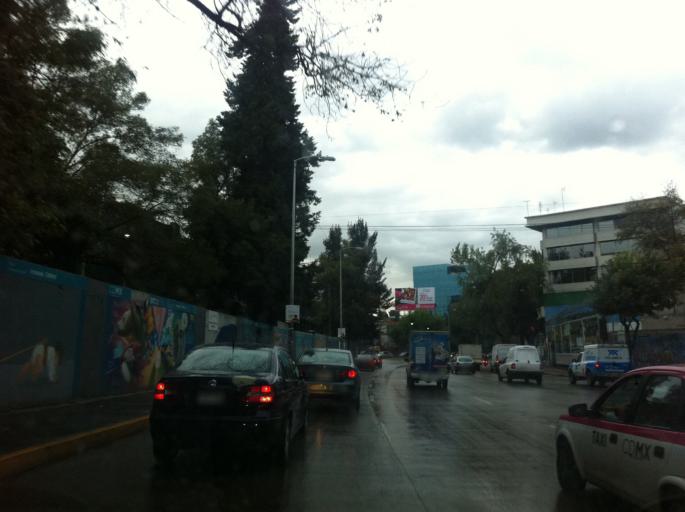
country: MX
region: Mexico City
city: Polanco
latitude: 19.4114
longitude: -99.1812
